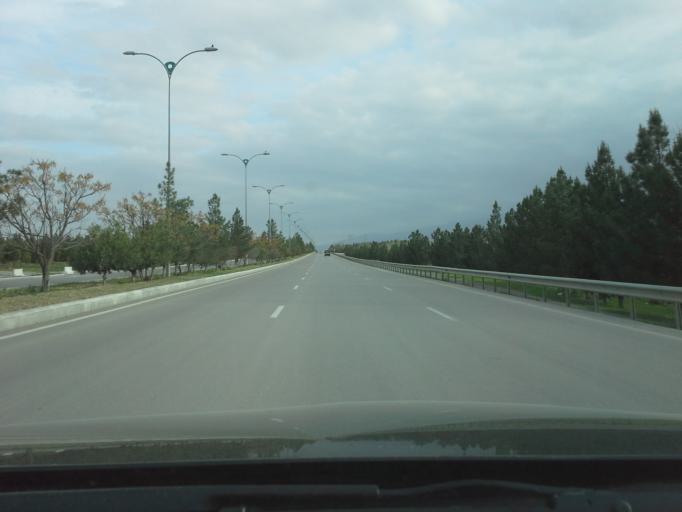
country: TM
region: Ahal
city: Abadan
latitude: 37.9565
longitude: 58.2259
